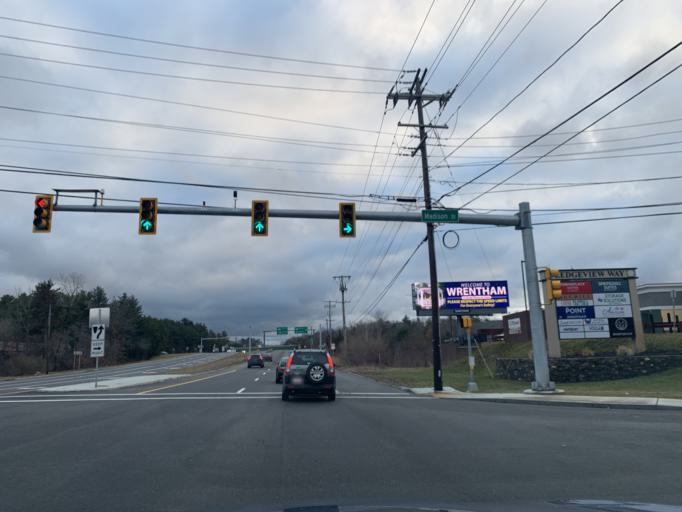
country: US
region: Massachusetts
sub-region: Norfolk County
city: Wrentham
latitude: 42.0417
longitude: -71.3048
